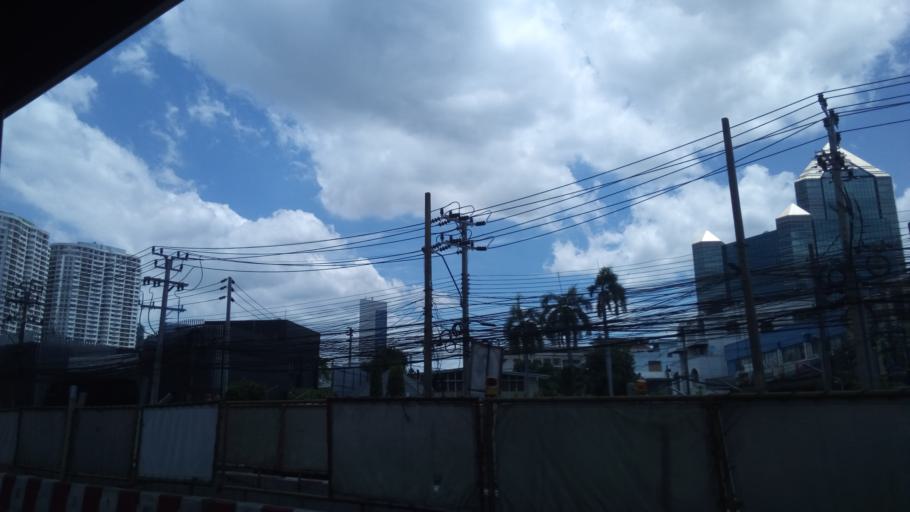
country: TH
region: Bangkok
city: Chatuchak
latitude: 13.8260
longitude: 100.5674
